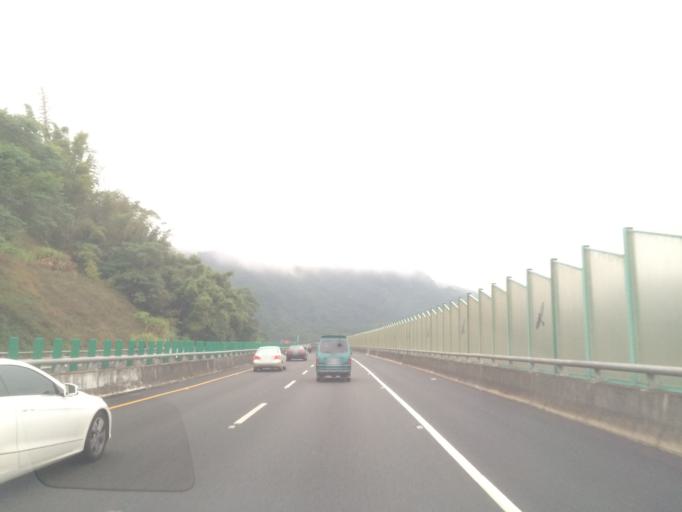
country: TW
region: Taiwan
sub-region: Nantou
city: Puli
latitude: 23.9950
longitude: 120.8515
